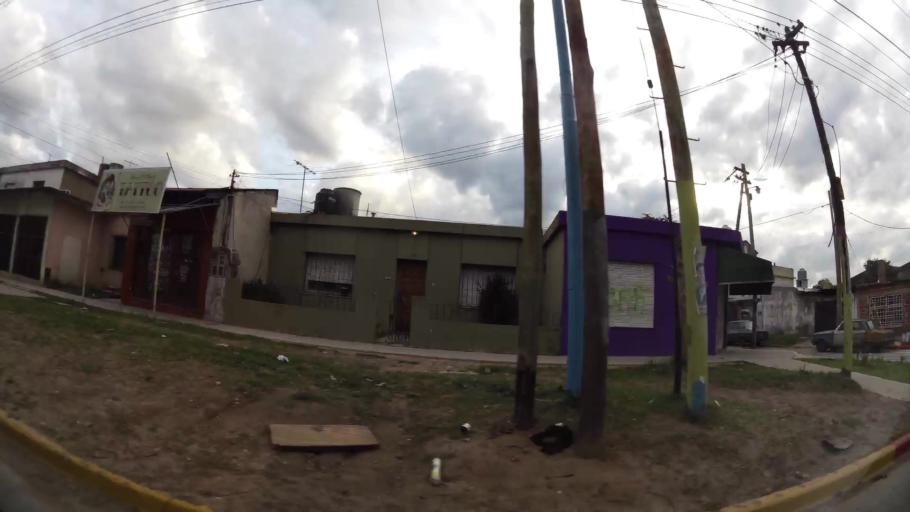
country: AR
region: Buenos Aires
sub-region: Partido de Quilmes
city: Quilmes
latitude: -34.7450
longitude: -58.2428
